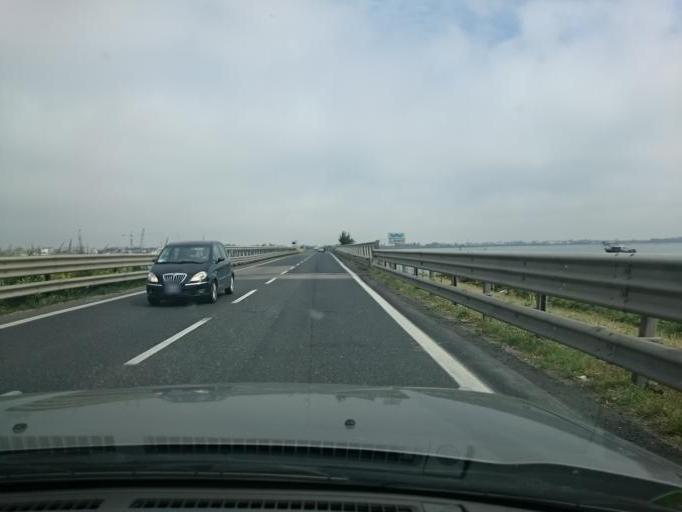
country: IT
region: Veneto
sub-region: Provincia di Venezia
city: Chioggia
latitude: 45.2030
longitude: 12.2547
